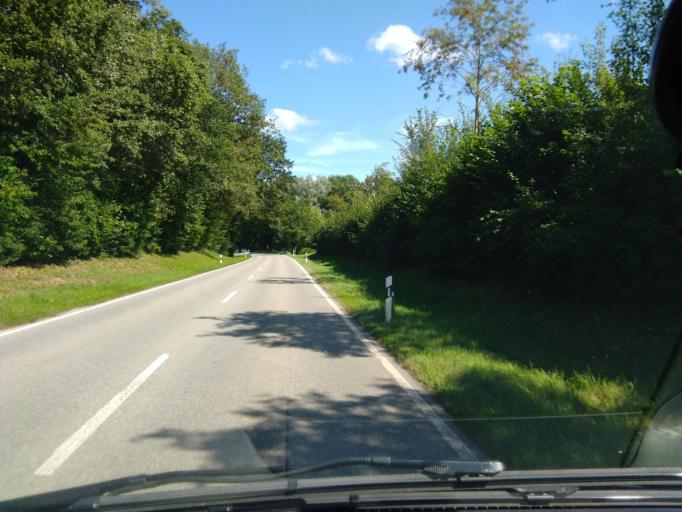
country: DE
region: Bavaria
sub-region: Upper Bavaria
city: Assling
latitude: 47.9914
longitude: 12.0307
